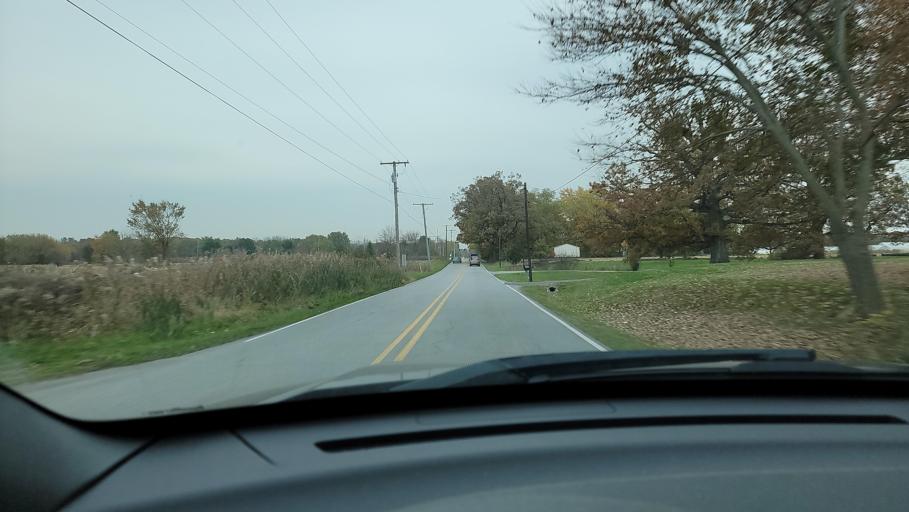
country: US
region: Indiana
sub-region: Lake County
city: Lake Station
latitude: 41.5543
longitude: -87.2215
